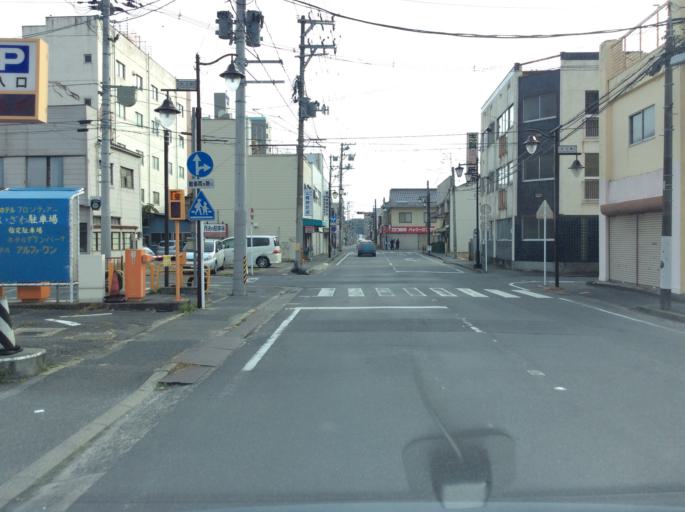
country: JP
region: Fukushima
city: Iwaki
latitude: 37.0572
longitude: 140.8964
